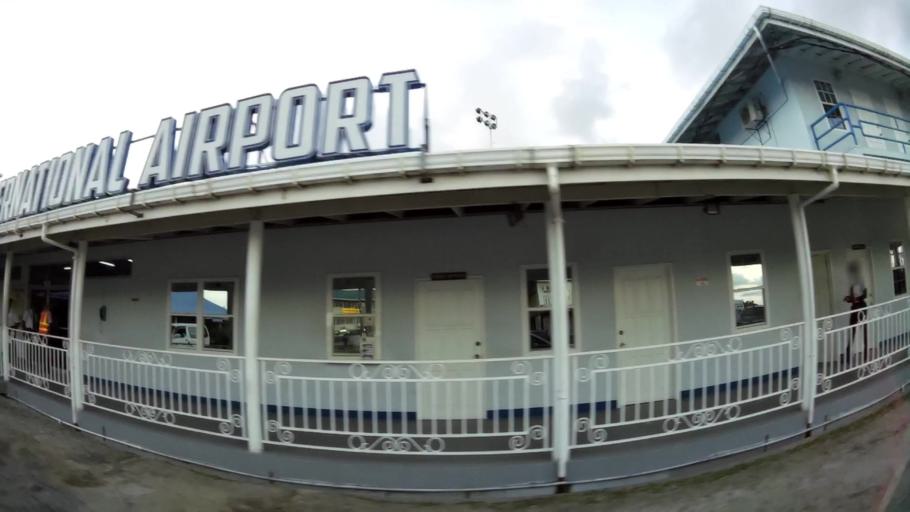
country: GY
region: Demerara-Mahaica
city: Georgetown
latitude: 6.8070
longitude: -58.1034
